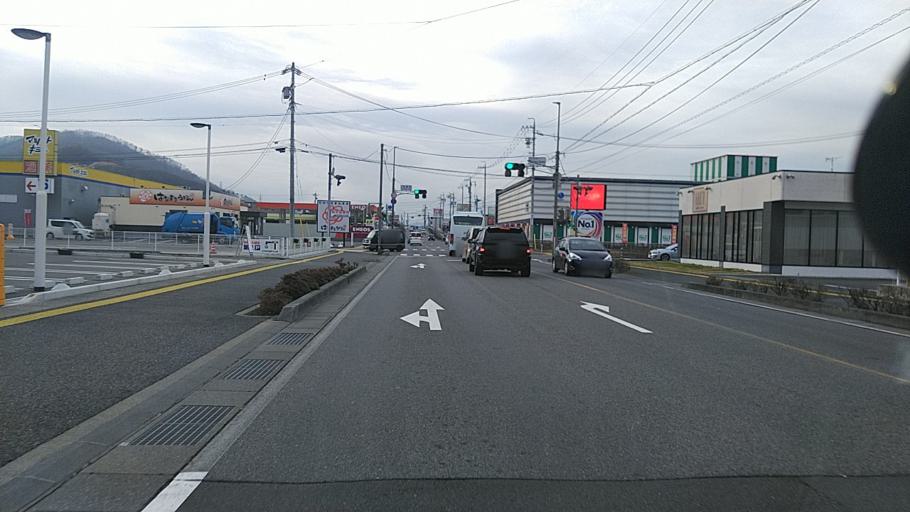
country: JP
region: Nagano
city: Matsumoto
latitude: 36.2194
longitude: 137.9797
